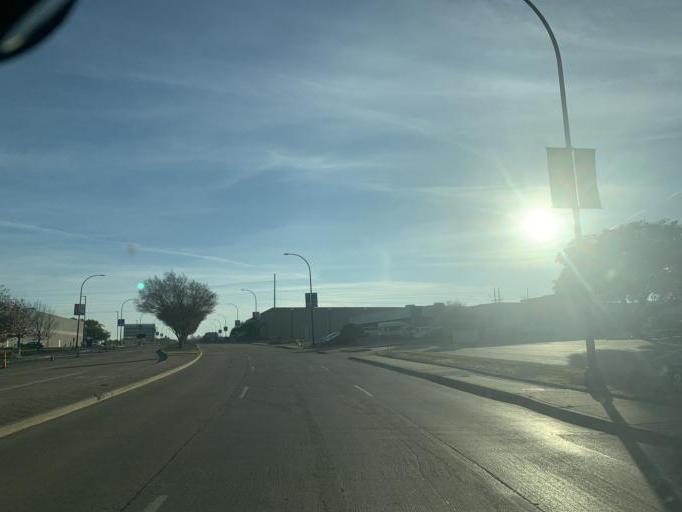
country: US
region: Texas
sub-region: Tarrant County
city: Arlington
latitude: 32.7480
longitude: -97.0763
